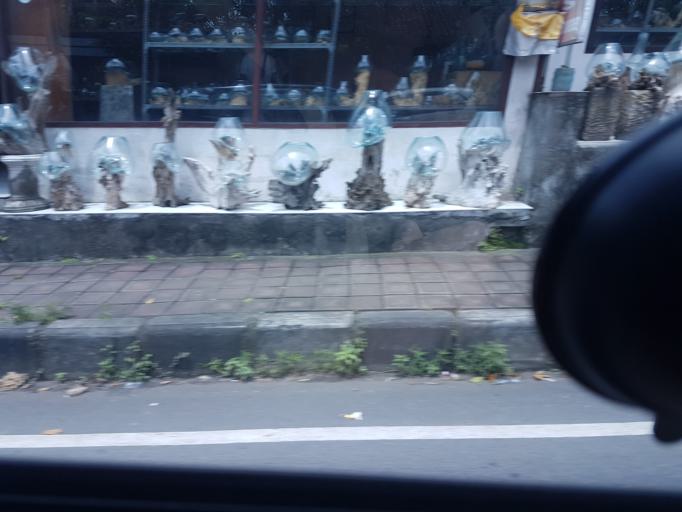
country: ID
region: Bali
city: Banjar Tebongkang
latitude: -8.5401
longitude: 115.2727
